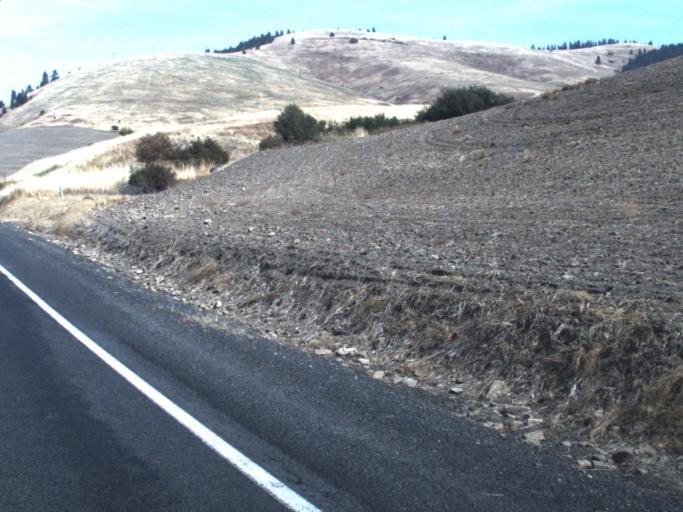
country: US
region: Idaho
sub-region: Benewah County
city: Plummer
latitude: 47.2508
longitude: -117.1318
